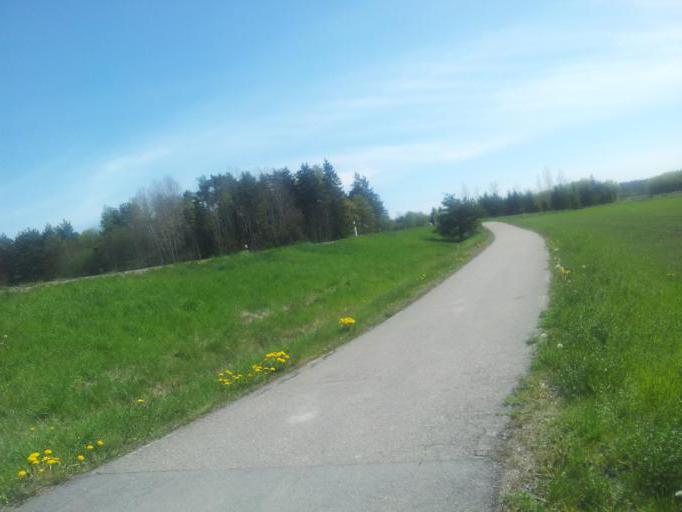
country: SE
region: Uppsala
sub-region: Uppsala Kommun
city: Saevja
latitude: 59.8558
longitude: 17.8219
